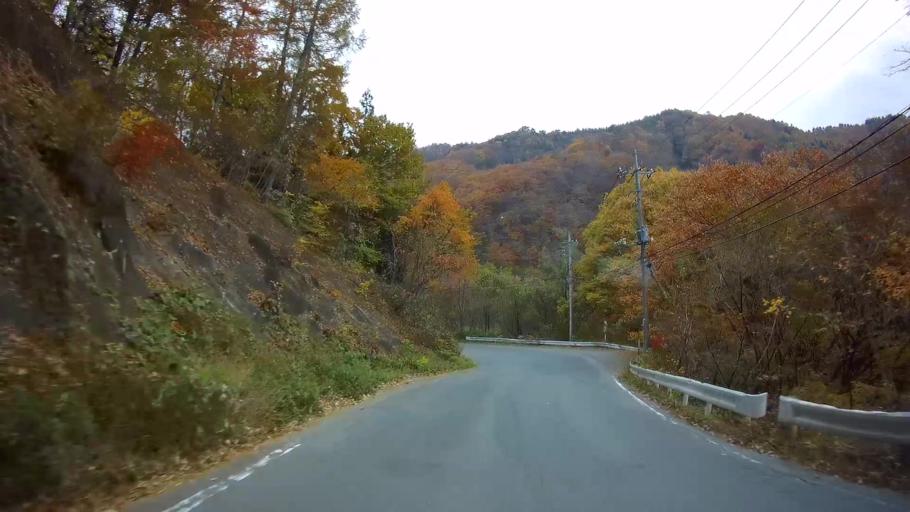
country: JP
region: Gunma
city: Nakanojomachi
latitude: 36.6376
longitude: 138.6514
